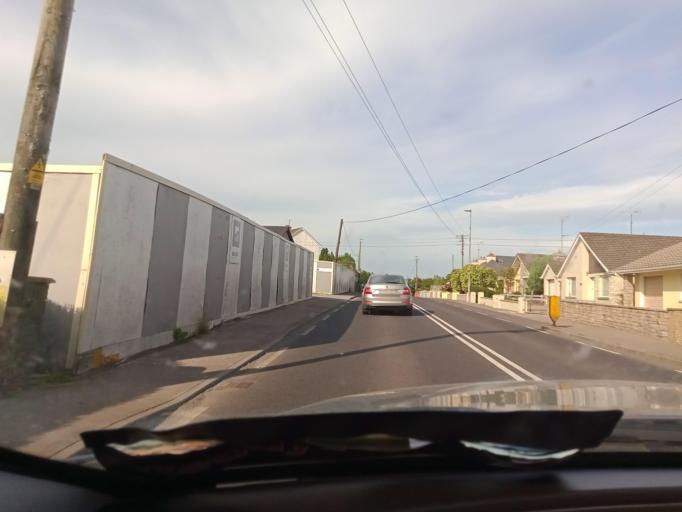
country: IE
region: Ulster
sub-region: An Cabhan
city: Cavan
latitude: 53.9347
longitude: -7.4063
